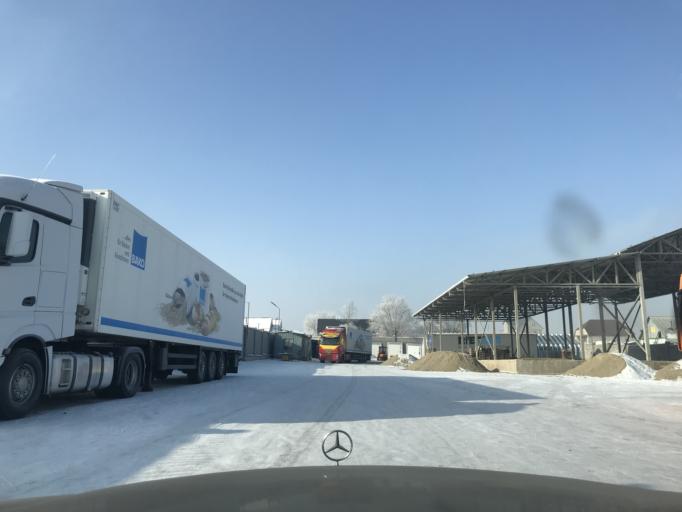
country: KZ
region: Almaty Oblysy
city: Burunday
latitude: 43.3376
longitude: 76.8323
